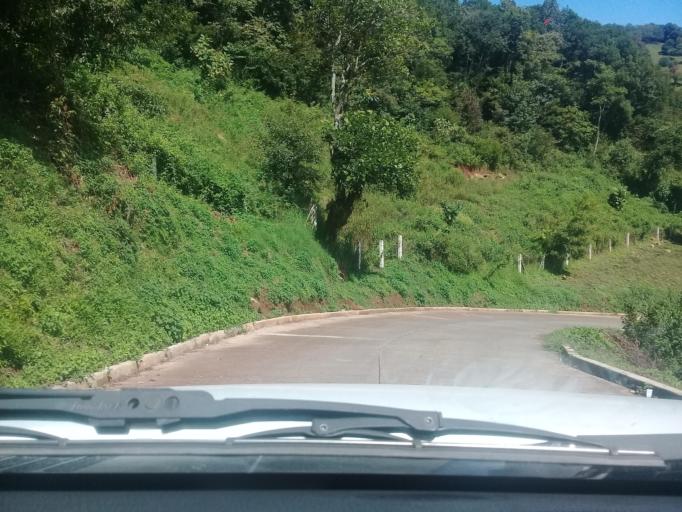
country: MX
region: Veracruz
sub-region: Tlalnelhuayocan
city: Otilpan
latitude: 19.5664
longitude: -96.9890
